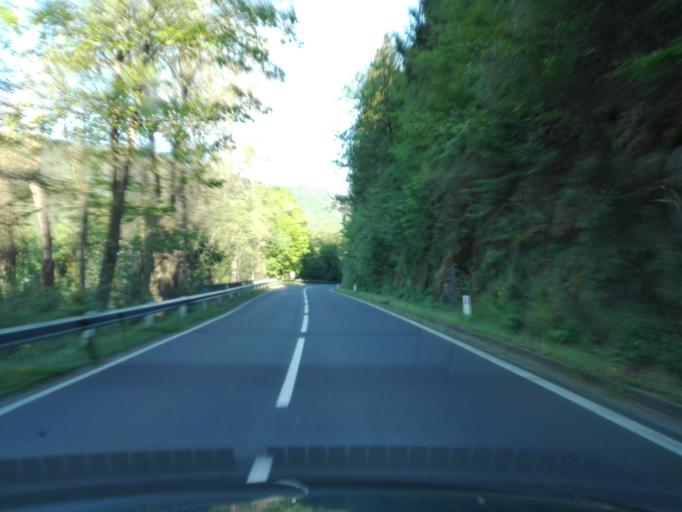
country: AT
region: Upper Austria
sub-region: Politischer Bezirk Rohrbach
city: Pfarrkirchen im Muehlkreis
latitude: 48.4657
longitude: 13.7851
